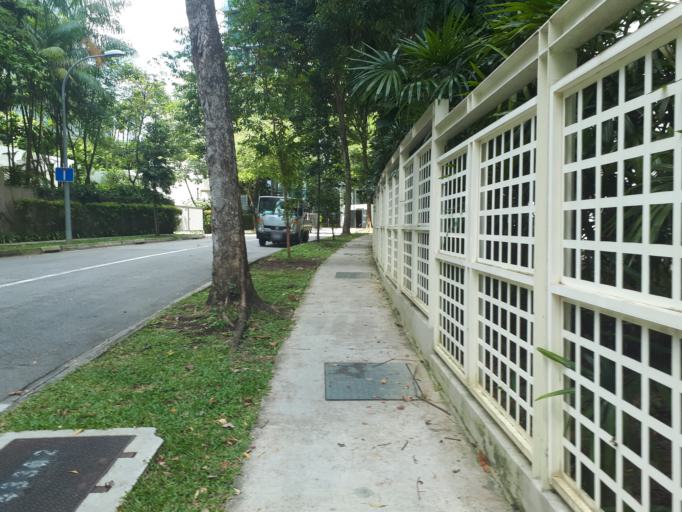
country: SG
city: Singapore
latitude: 1.2975
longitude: 103.8371
